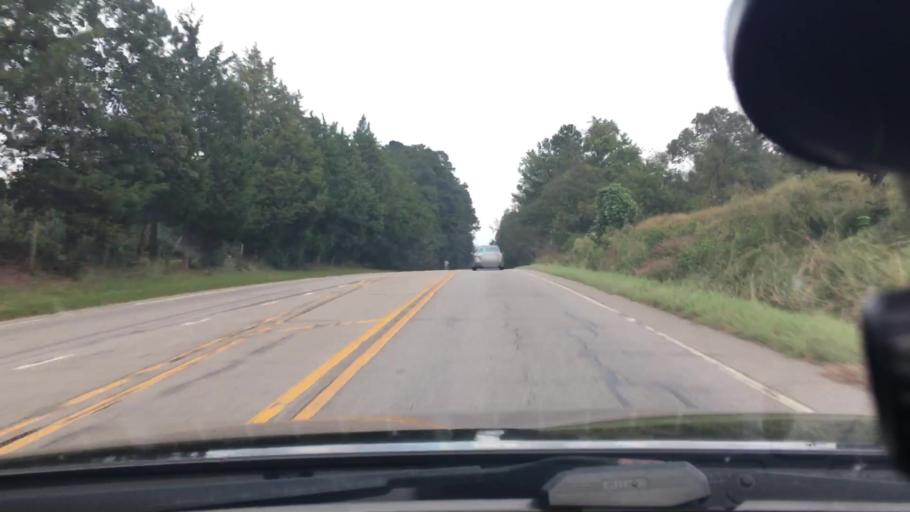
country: US
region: North Carolina
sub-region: Moore County
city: Carthage
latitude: 35.3694
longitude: -79.3082
